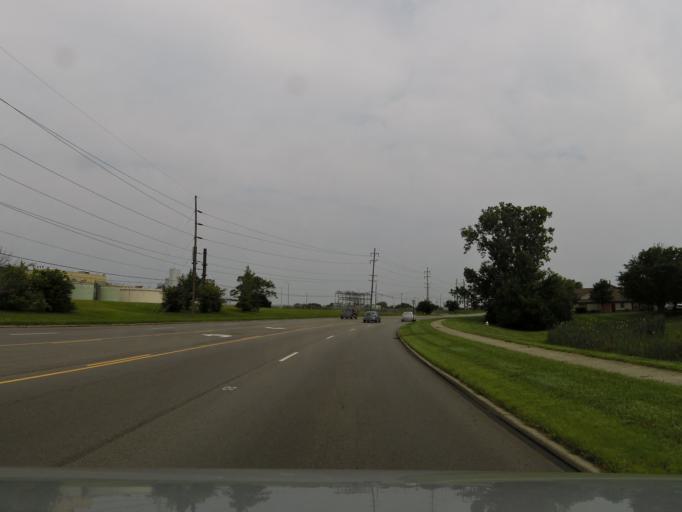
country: US
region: Ohio
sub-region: Montgomery County
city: Kettering
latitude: 39.7083
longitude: -84.1239
